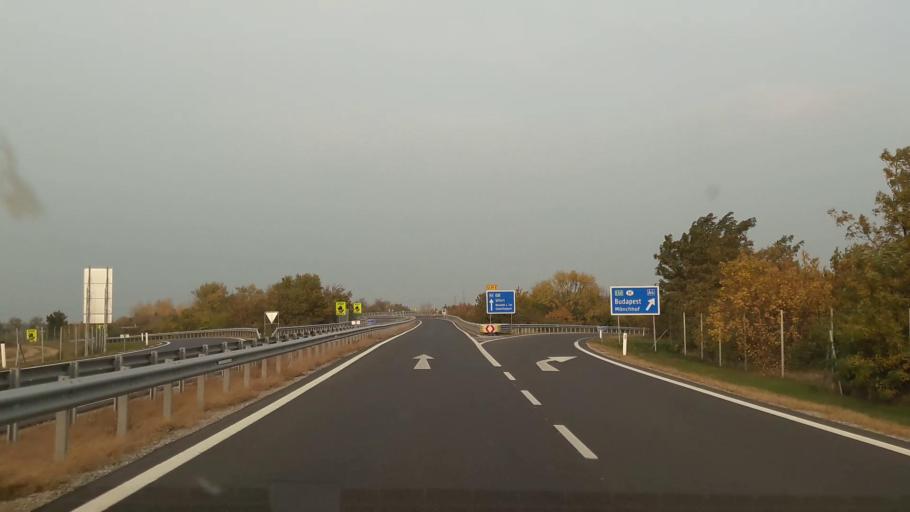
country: AT
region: Burgenland
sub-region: Politischer Bezirk Neusiedl am See
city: Gols
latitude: 47.9456
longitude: 16.9321
